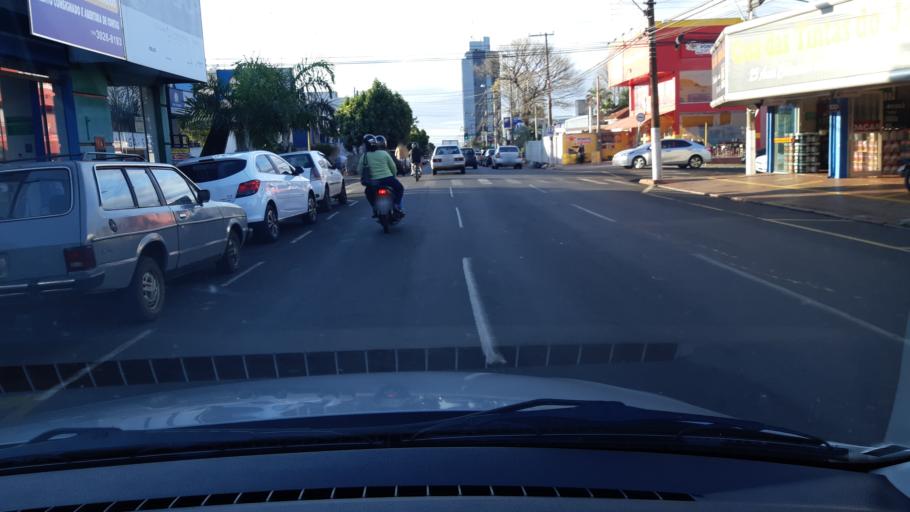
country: BR
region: Sao Paulo
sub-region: Ourinhos
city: Ourinhos
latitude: -22.9810
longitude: -49.8665
